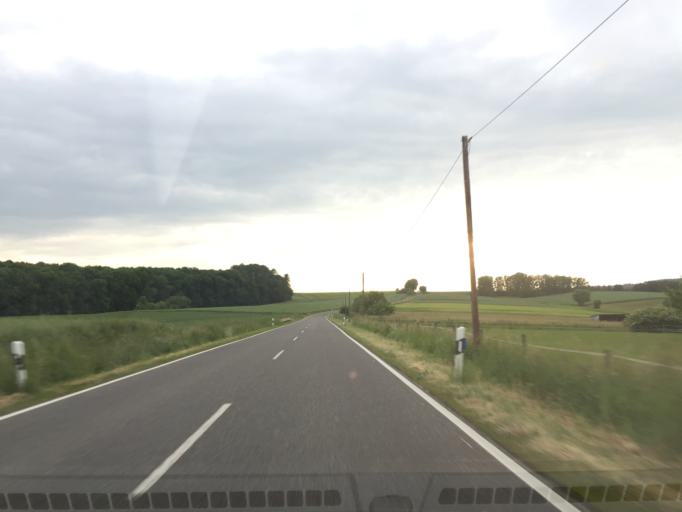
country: DE
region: Hesse
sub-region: Regierungsbezirk Giessen
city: Elz
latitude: 50.4521
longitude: 8.0210
